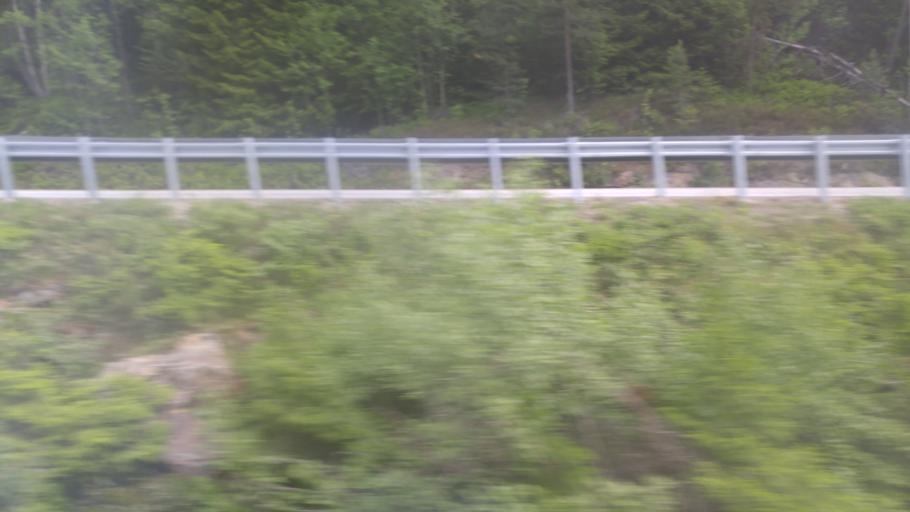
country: NO
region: Sor-Trondelag
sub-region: Selbu
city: Mebonden
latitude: 62.9794
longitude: 10.9437
